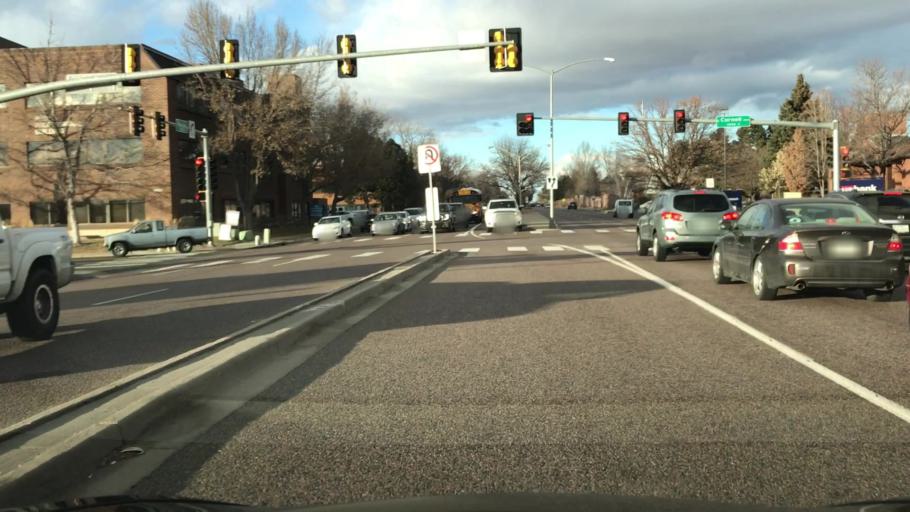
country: US
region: Colorado
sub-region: Adams County
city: Aurora
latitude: 39.6614
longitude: -104.8473
